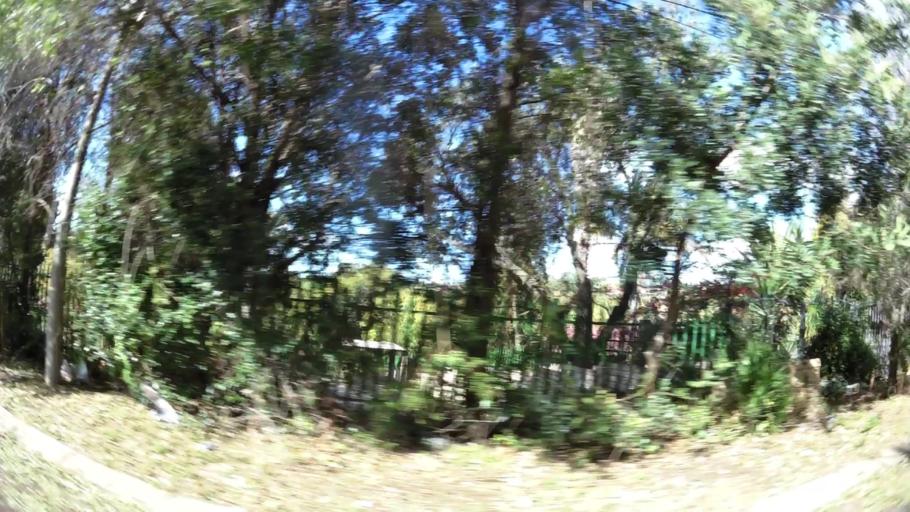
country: ZA
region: Gauteng
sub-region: City of Johannesburg Metropolitan Municipality
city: Roodepoort
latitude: -26.1164
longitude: 27.8426
